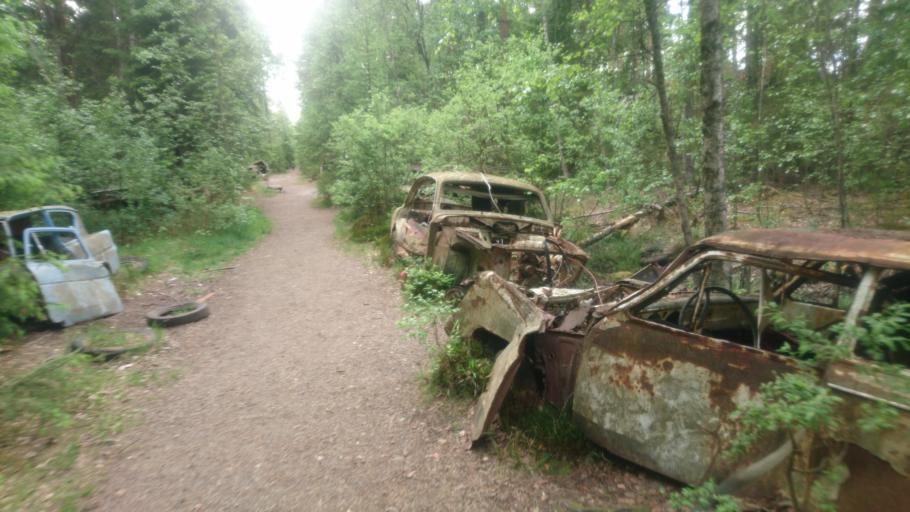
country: SE
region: Blekinge
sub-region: Olofstroms Kommun
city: Olofstroem
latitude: 56.4664
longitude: 14.6522
